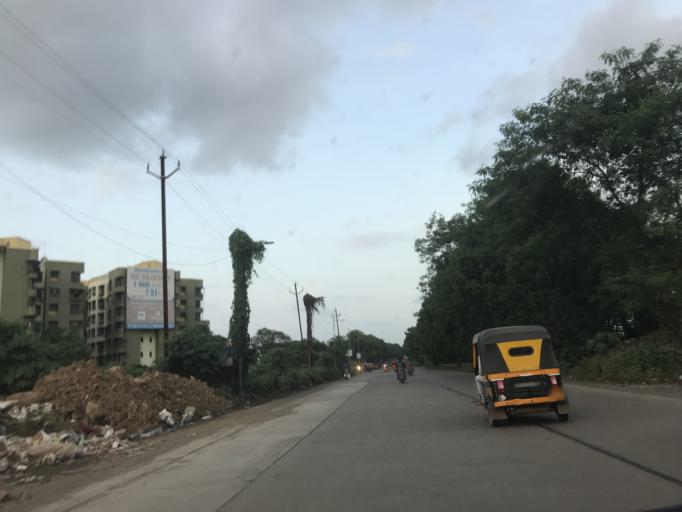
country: IN
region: Maharashtra
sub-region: Thane
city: Thane
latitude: 19.2252
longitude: 72.9959
